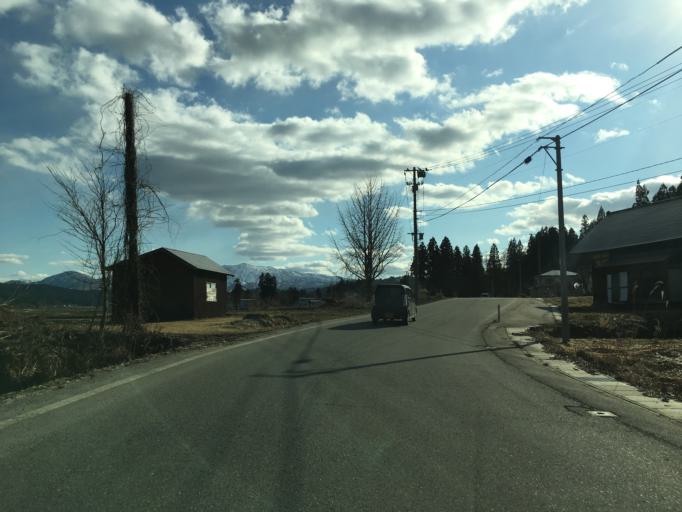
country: JP
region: Yamagata
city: Yonezawa
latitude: 37.9662
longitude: 139.9918
